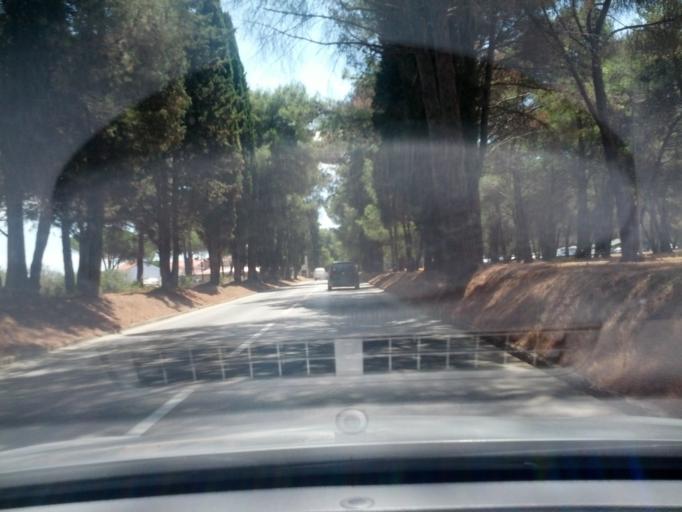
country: HR
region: Istarska
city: Fazana
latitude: 44.9183
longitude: 13.8111
